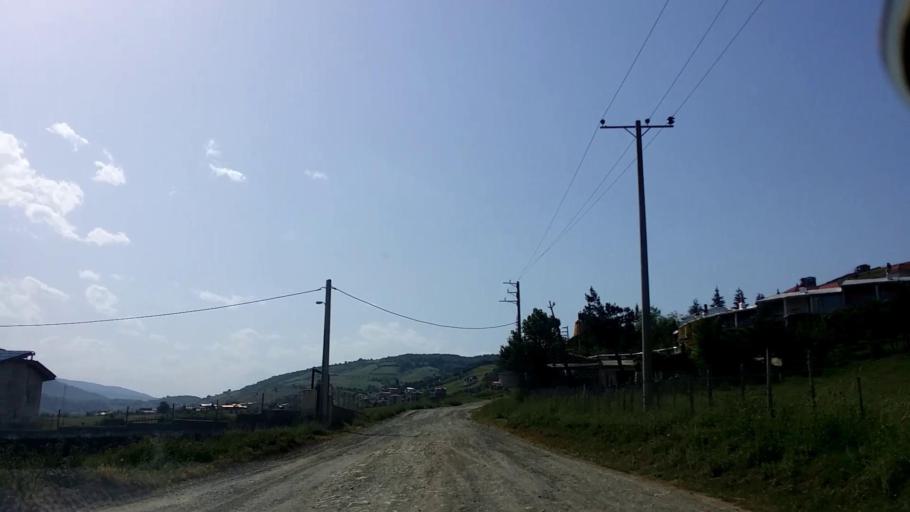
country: IR
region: Mazandaran
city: `Abbasabad
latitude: 36.5437
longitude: 51.1996
